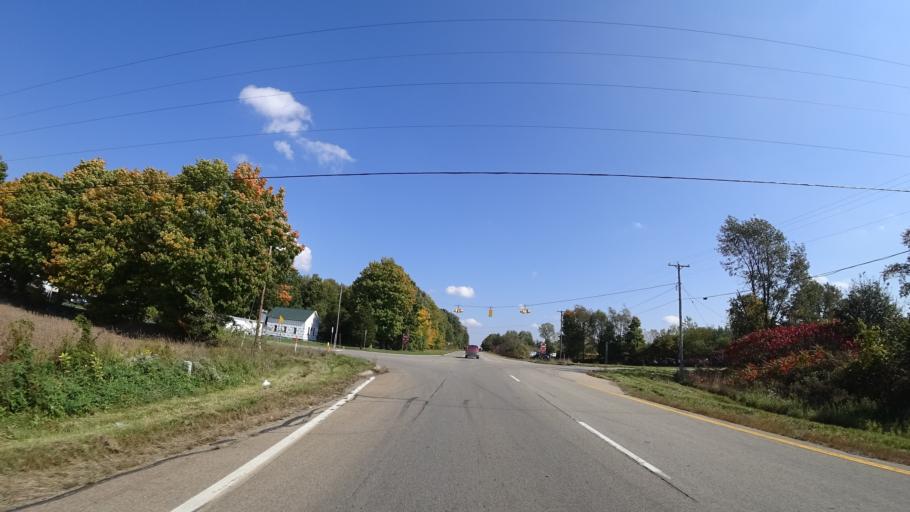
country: US
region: Michigan
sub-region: Calhoun County
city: Homer
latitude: 42.1612
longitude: -84.7511
